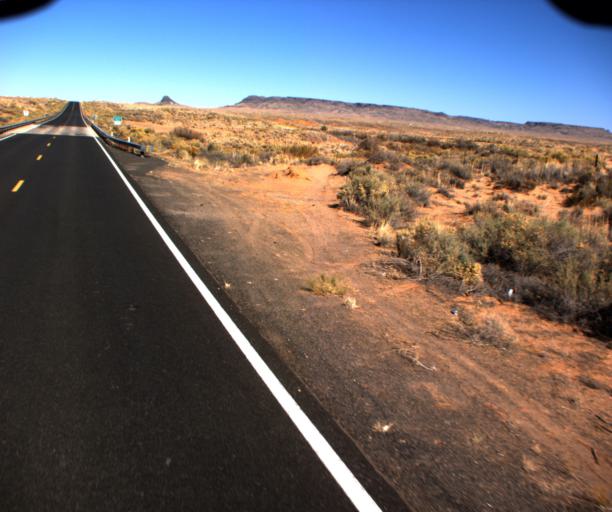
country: US
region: Arizona
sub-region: Navajo County
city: Dilkon
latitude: 35.3582
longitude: -110.4245
